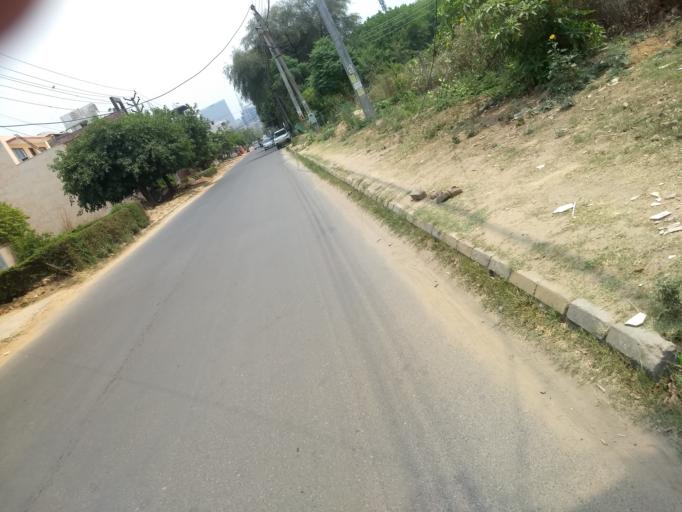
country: IN
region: Haryana
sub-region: Gurgaon
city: Gurgaon
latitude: 28.4623
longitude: 77.0926
